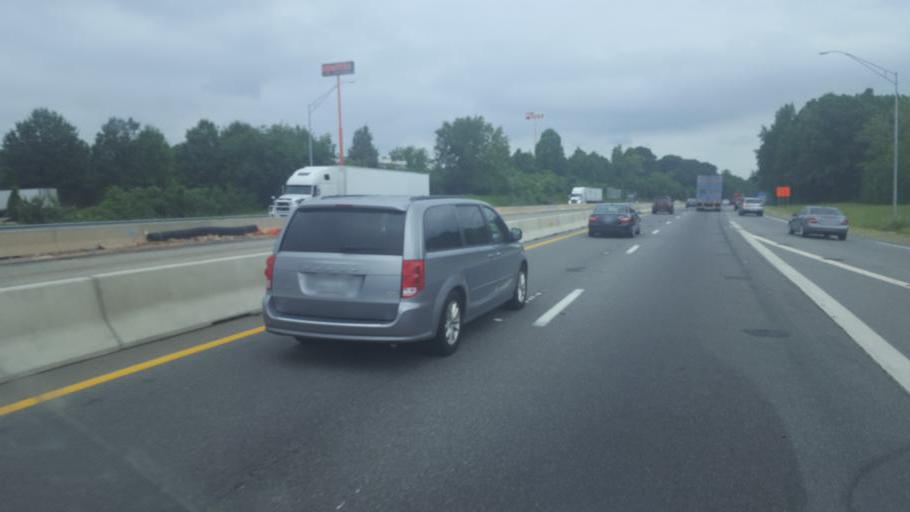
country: US
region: North Carolina
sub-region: Iredell County
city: Mooresville
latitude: 35.5964
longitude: -80.8600
